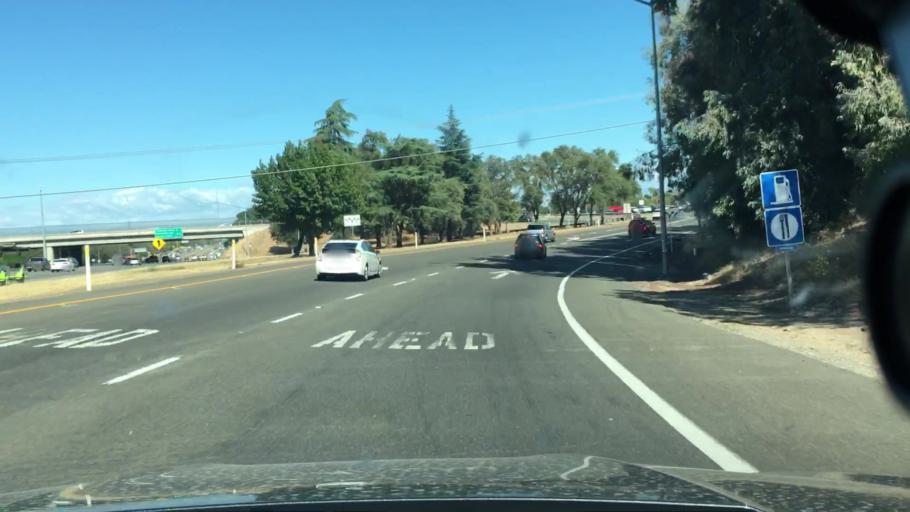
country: US
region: California
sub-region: Sacramento County
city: Foothill Farms
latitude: 38.6810
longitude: -121.3378
